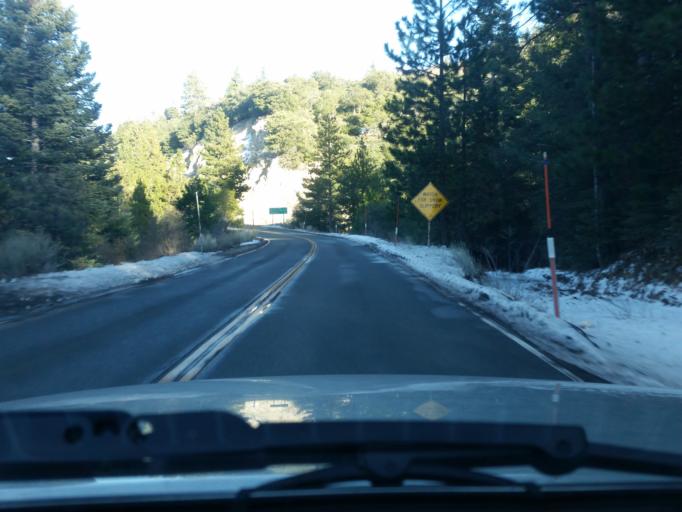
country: US
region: California
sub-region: San Bernardino County
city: Big Bear Lake
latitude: 34.1499
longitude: -116.9770
